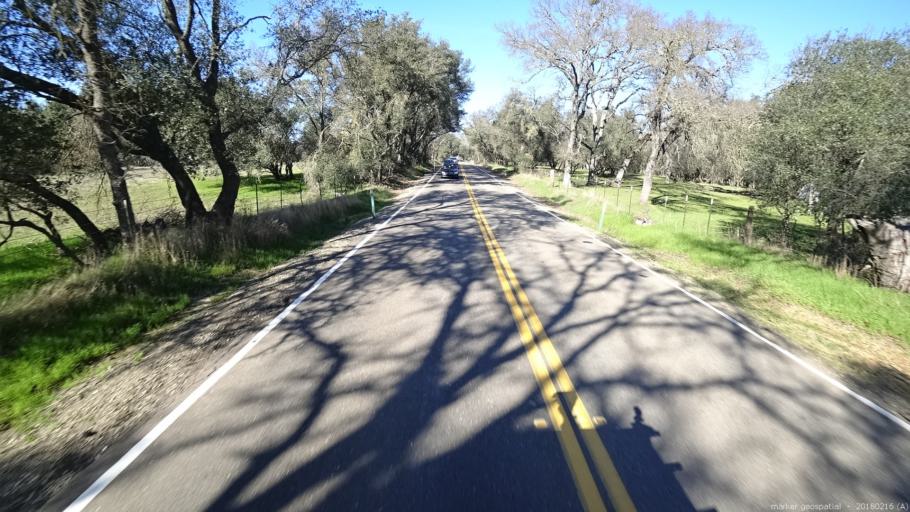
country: US
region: California
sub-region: Sacramento County
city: Rancho Murieta
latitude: 38.5278
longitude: -121.1041
